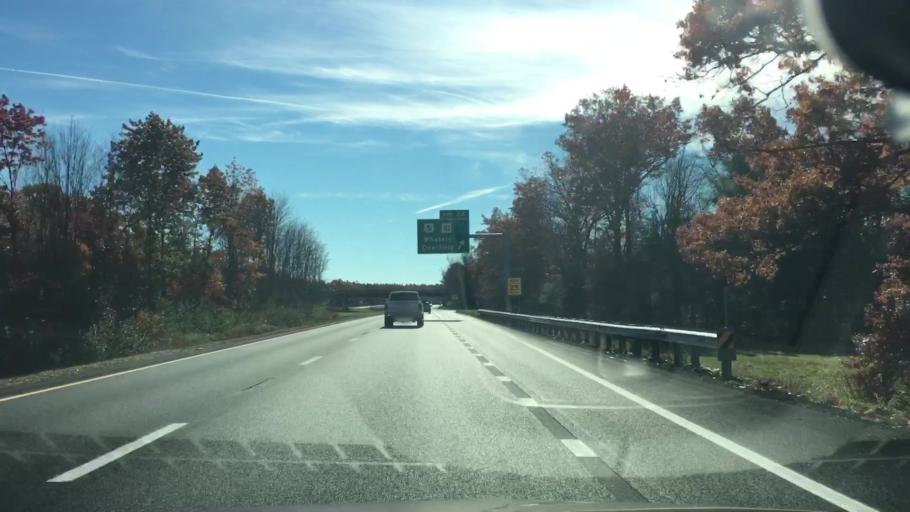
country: US
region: Massachusetts
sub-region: Franklin County
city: South Deerfield
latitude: 42.4701
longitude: -72.6170
